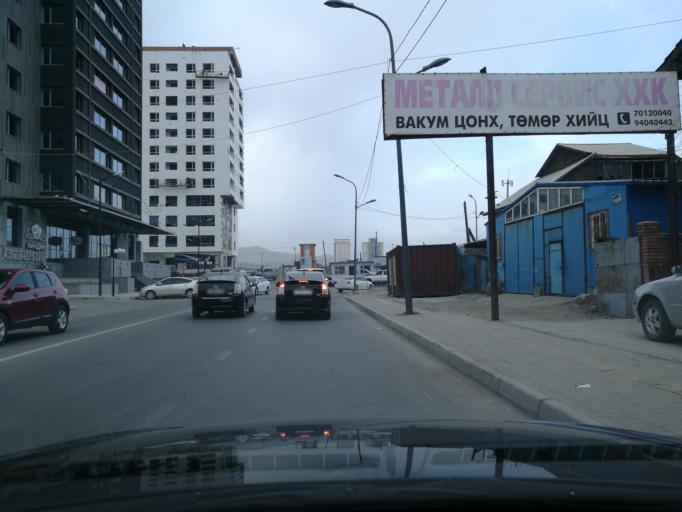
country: MN
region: Ulaanbaatar
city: Ulaanbaatar
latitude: 47.9319
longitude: 106.9138
